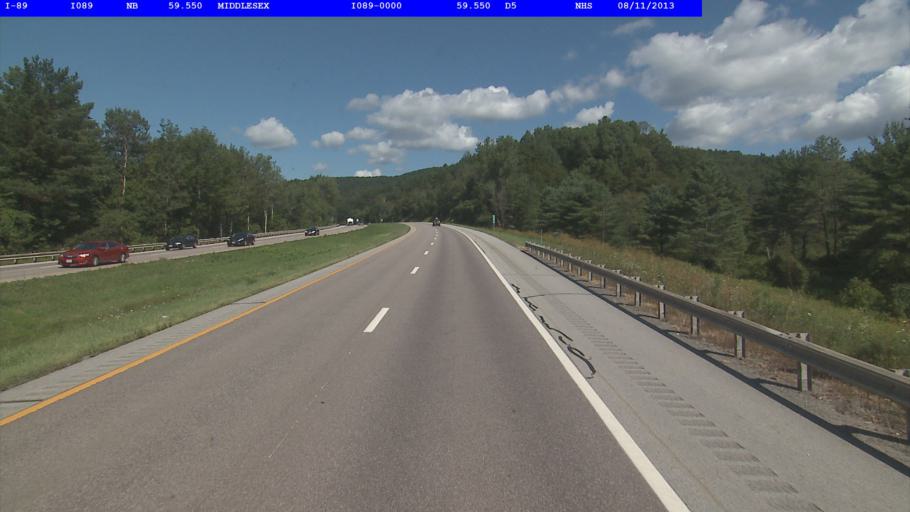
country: US
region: Vermont
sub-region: Washington County
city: Waterbury
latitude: 44.3088
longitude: -72.6924
